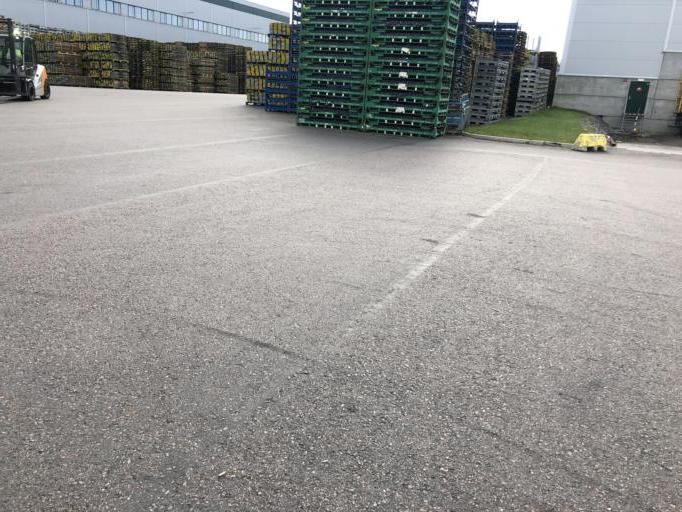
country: SE
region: Vaestra Goetaland
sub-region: Goteborg
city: Majorna
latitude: 57.7389
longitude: 11.8625
